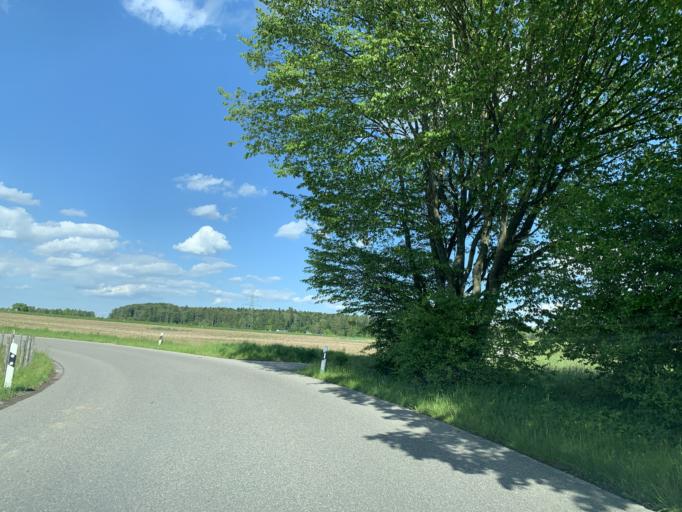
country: CH
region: Zurich
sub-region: Bezirk Pfaeffikon
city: Weisslingen
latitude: 47.4489
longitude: 8.7424
